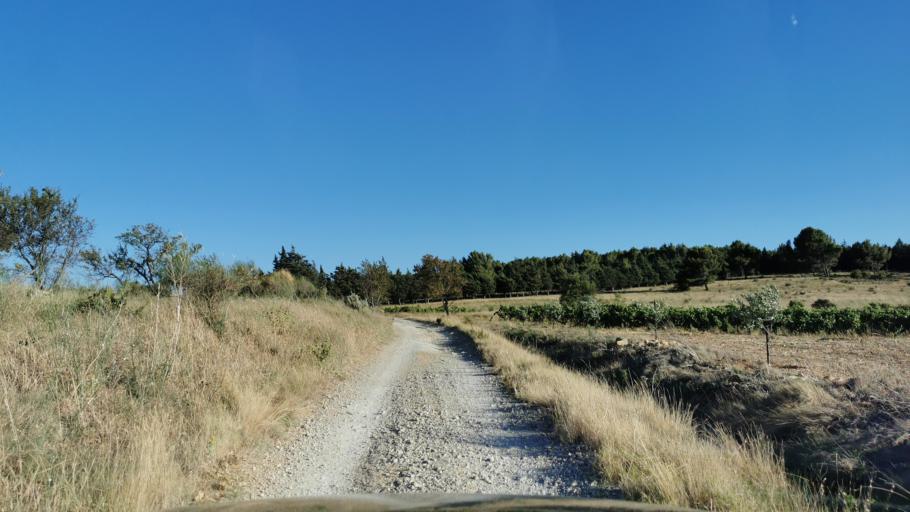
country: FR
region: Languedoc-Roussillon
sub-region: Departement de l'Aude
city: Ouveillan
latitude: 43.2722
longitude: 2.9769
